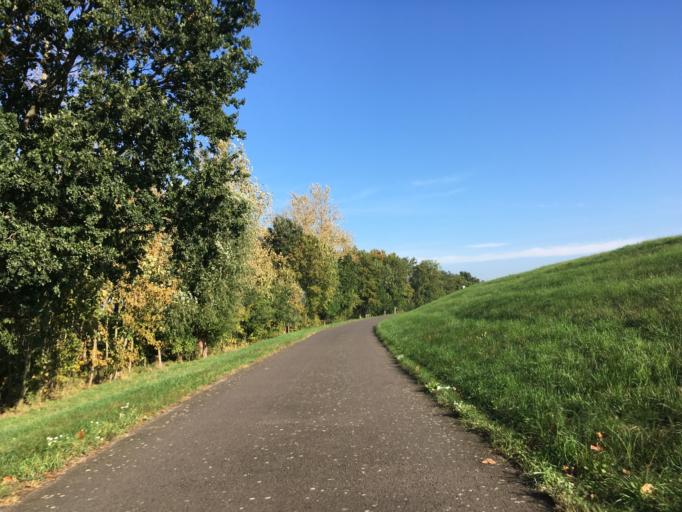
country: PL
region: Lubusz
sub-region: Powiat gorzowski
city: Kostrzyn nad Odra
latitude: 52.5521
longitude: 14.6106
